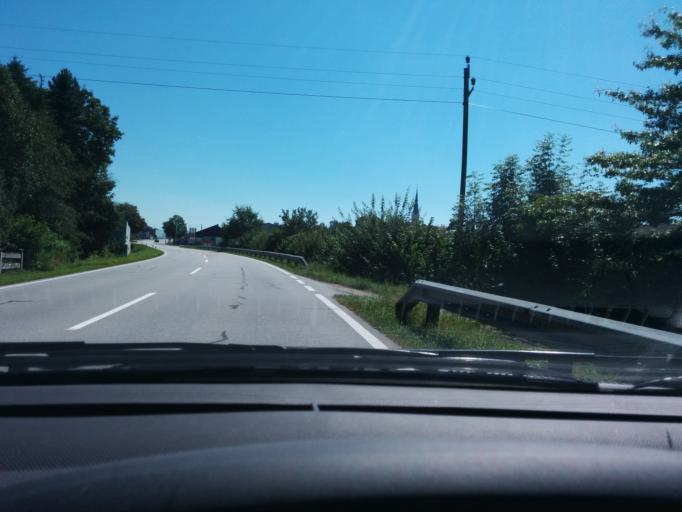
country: AT
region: Upper Austria
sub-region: Politischer Bezirk Rohrbach
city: Ulrichsberg
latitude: 48.6799
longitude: 13.9057
